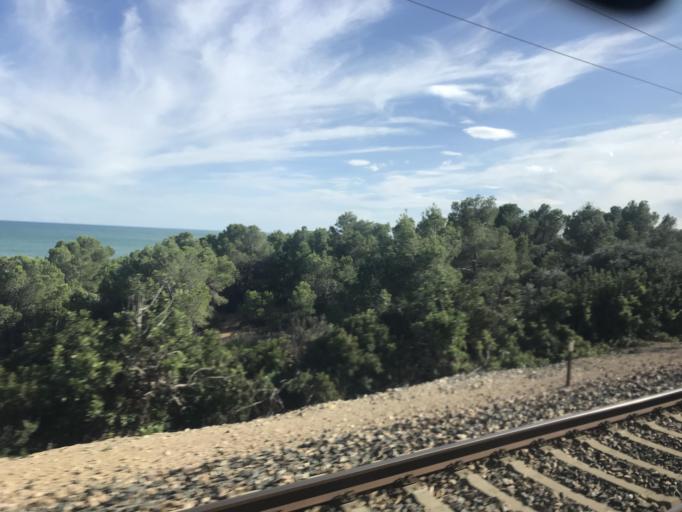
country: ES
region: Catalonia
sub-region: Provincia de Tarragona
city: l'Ametlla de Mar
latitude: 40.8559
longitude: 0.7660
